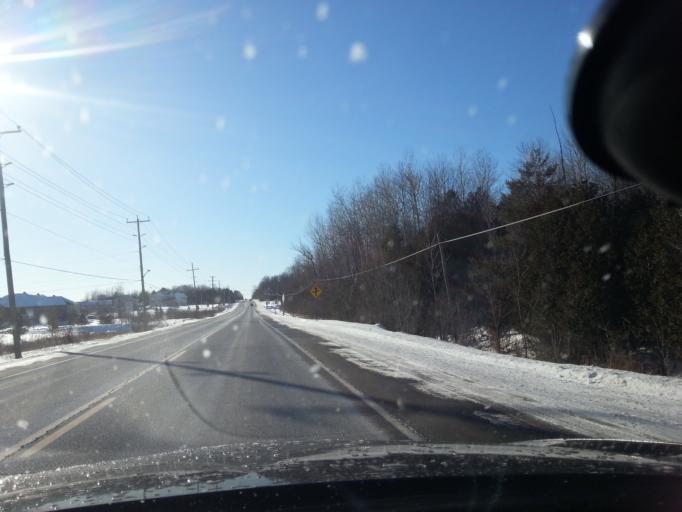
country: CA
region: Ontario
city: Ottawa
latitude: 45.2903
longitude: -75.5454
